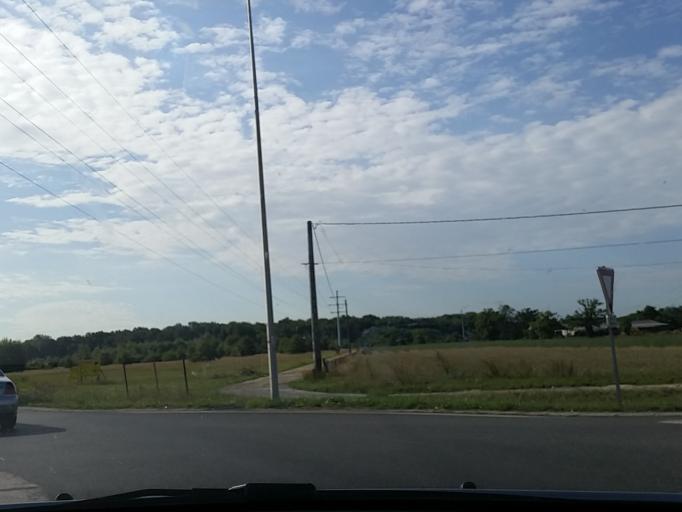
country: FR
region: Centre
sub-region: Departement du Loir-et-Cher
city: Romorantin-Lanthenay
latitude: 47.3634
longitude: 1.7116
